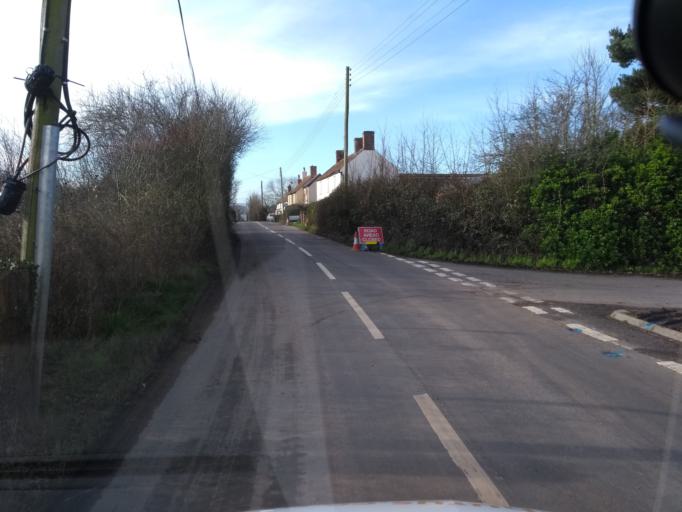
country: GB
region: England
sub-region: Somerset
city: Creech Saint Michael
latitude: 51.0171
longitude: -2.9825
